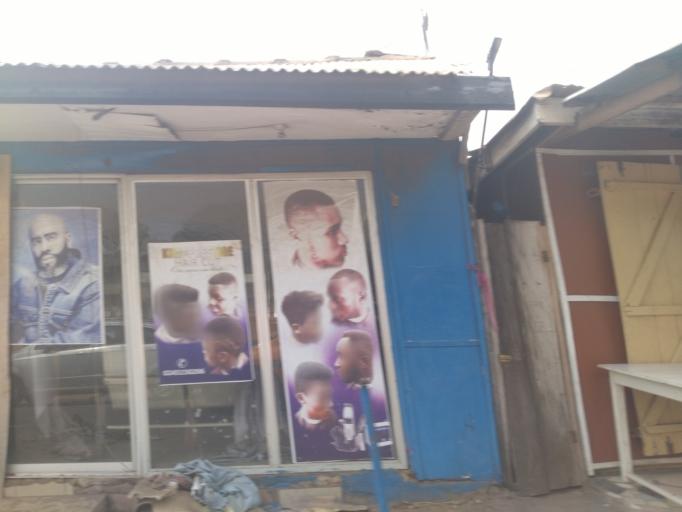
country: GH
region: Greater Accra
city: Accra
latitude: 5.5521
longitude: -0.1809
